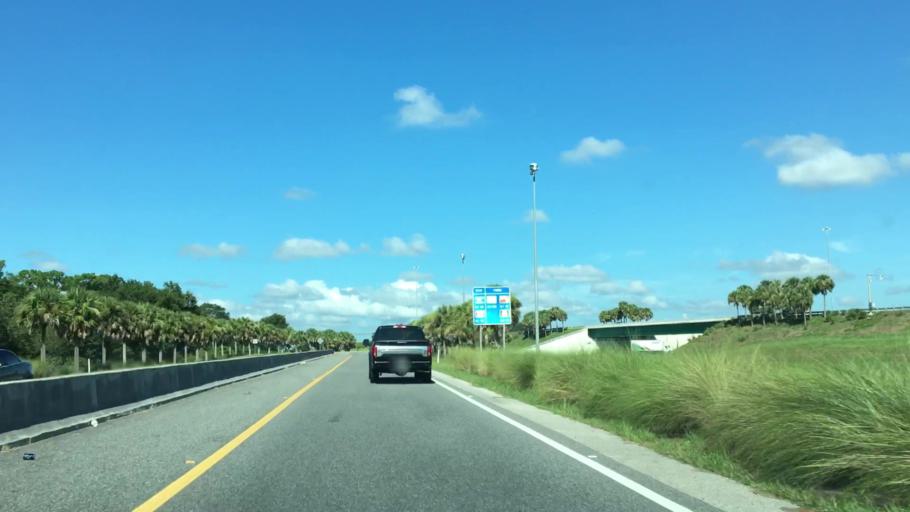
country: US
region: Florida
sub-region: Seminole County
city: Lake Mary
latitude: 28.7969
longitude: -81.3298
